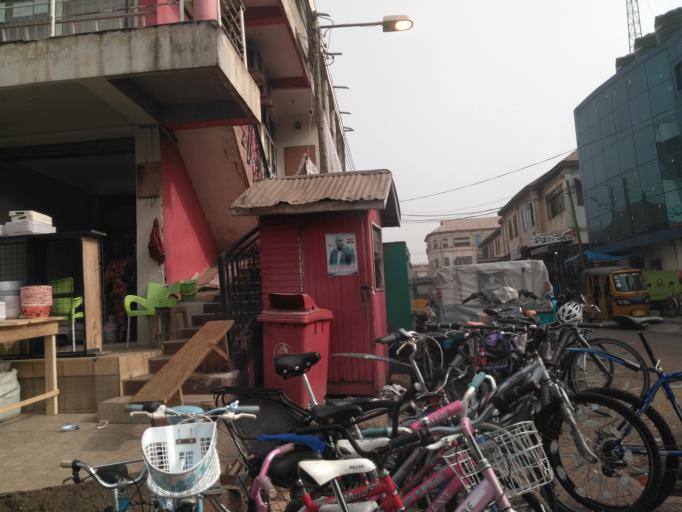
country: GH
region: Ashanti
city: Kumasi
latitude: 6.6993
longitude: -1.6170
